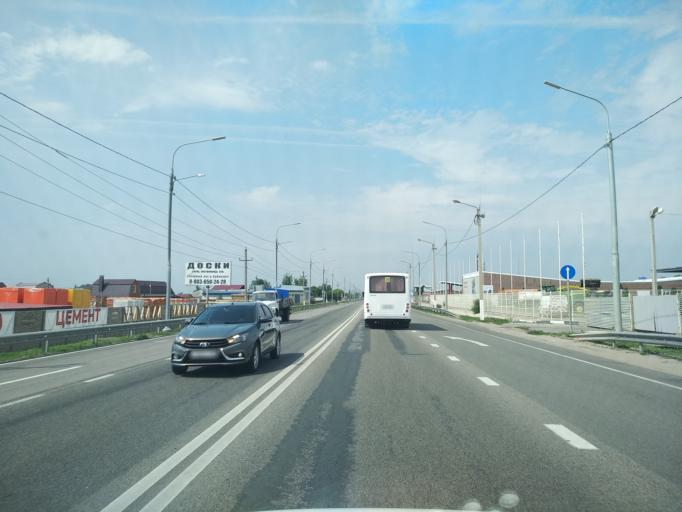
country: RU
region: Voronezj
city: Somovo
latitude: 51.6929
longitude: 39.3761
